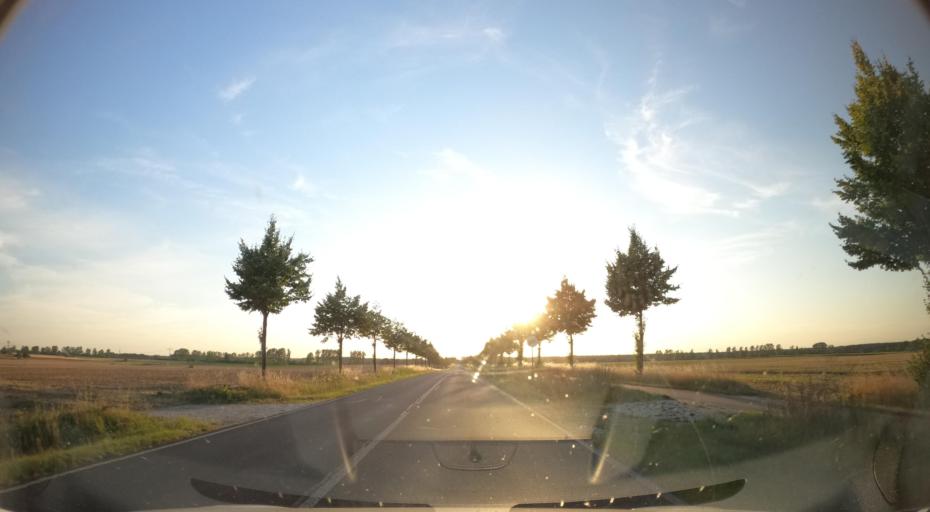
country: DE
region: Mecklenburg-Vorpommern
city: Viereck
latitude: 53.4978
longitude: 14.0746
